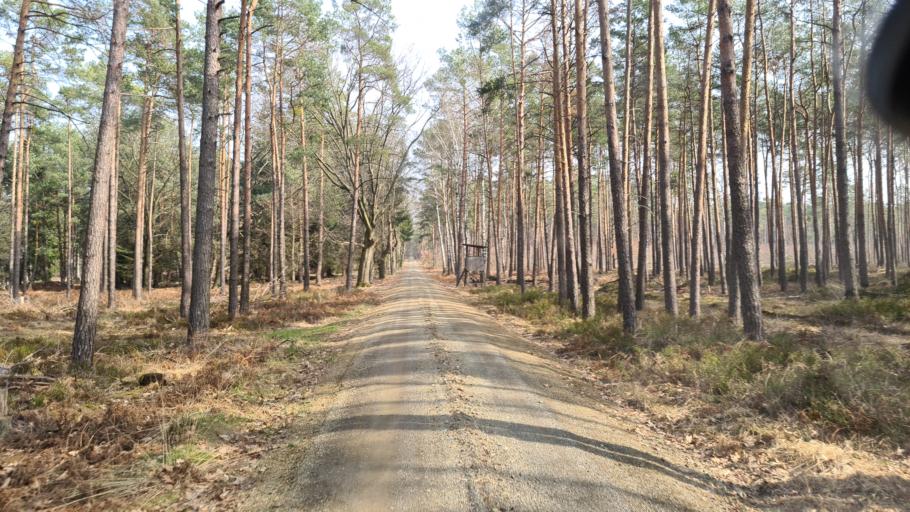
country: DE
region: Brandenburg
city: Trobitz
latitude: 51.6302
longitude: 13.4290
